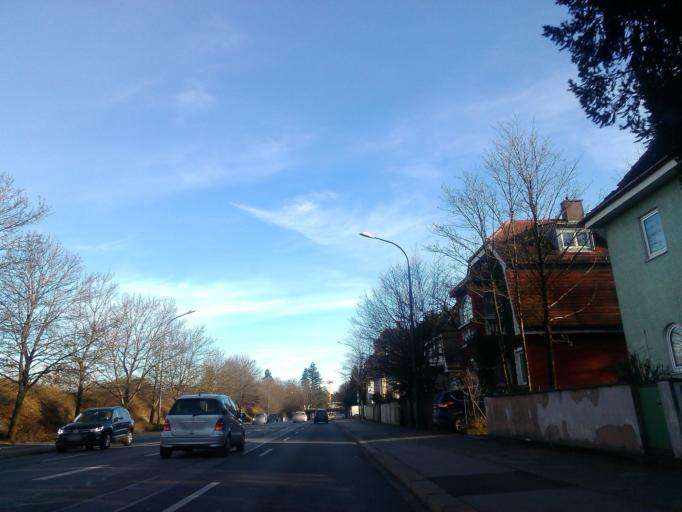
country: DE
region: Bavaria
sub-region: Upper Bavaria
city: Pasing
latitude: 48.1640
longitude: 11.4813
